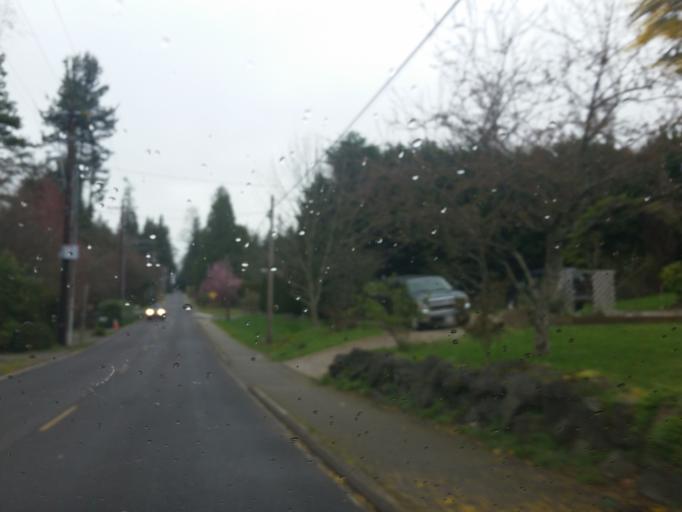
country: US
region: Washington
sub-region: Snohomish County
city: Meadowdale
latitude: 47.8427
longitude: -122.3359
